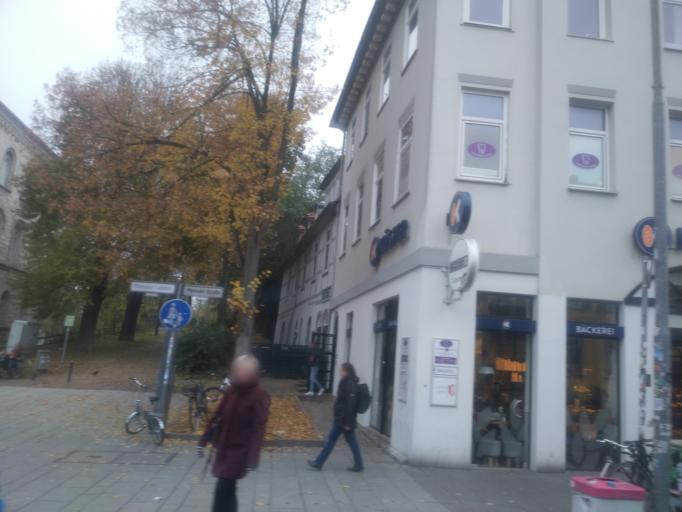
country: DE
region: Lower Saxony
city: Goettingen
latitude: 51.5376
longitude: 9.9342
